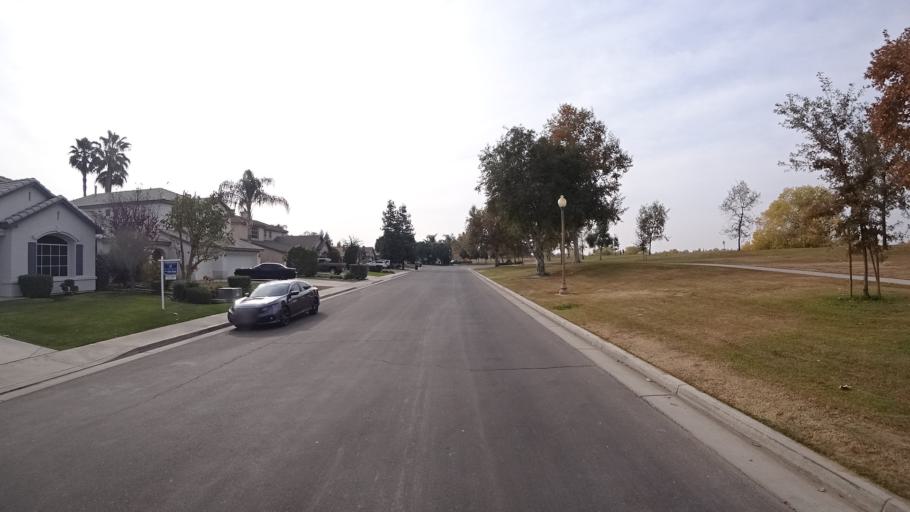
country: US
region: California
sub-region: Kern County
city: Rosedale
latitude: 35.3486
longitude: -119.1343
